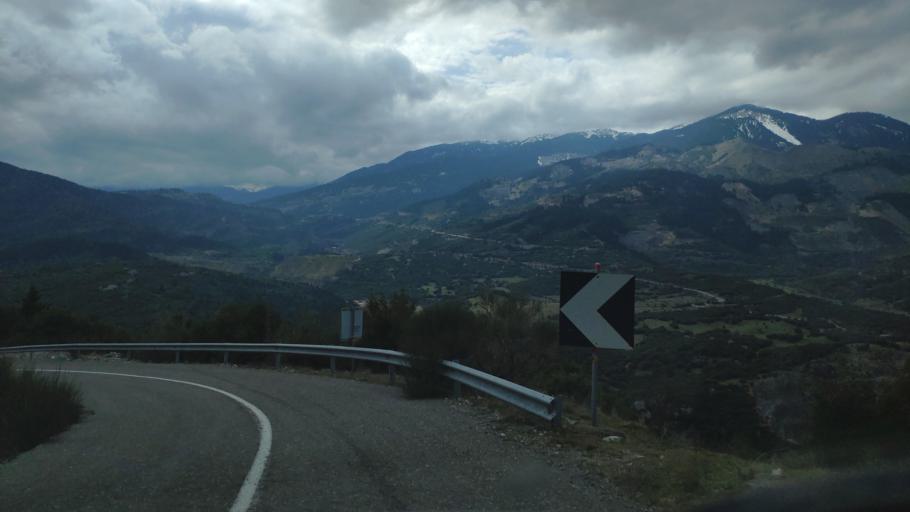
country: GR
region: Central Greece
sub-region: Nomos Fokidos
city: Amfissa
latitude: 38.6451
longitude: 22.4195
